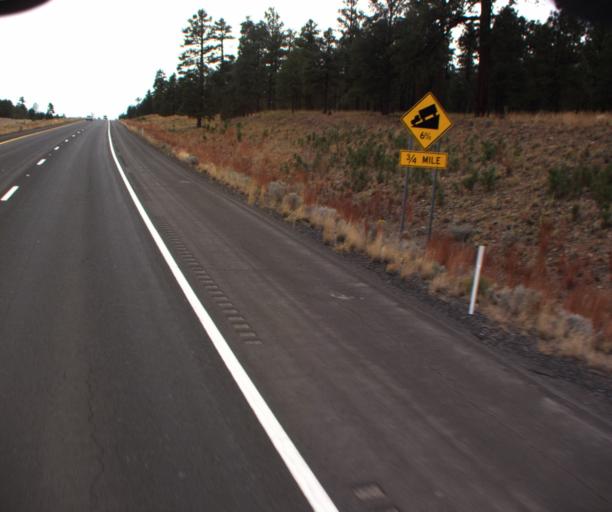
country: US
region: Arizona
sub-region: Coconino County
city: Flagstaff
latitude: 35.3638
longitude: -111.5718
